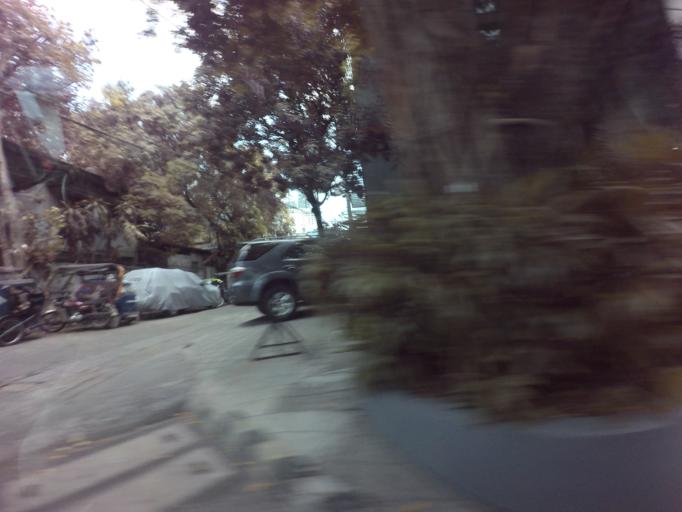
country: PH
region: Metro Manila
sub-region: Makati City
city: Makati City
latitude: 14.5649
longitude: 121.0330
